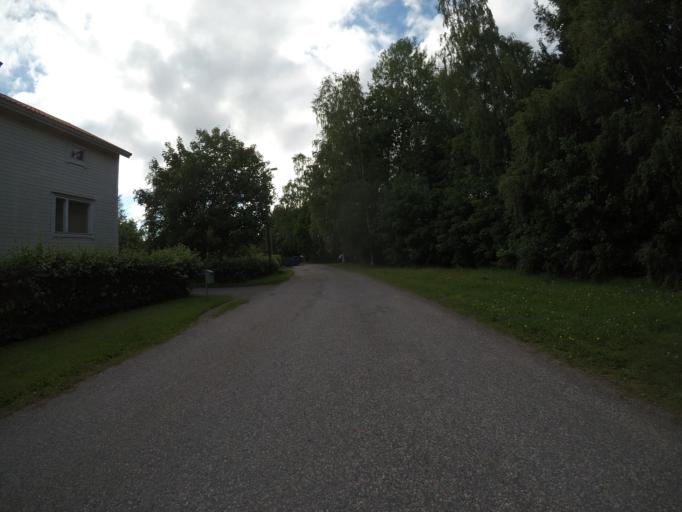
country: FI
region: Haeme
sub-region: Haemeenlinna
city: Haemeenlinna
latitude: 60.9895
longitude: 24.4489
